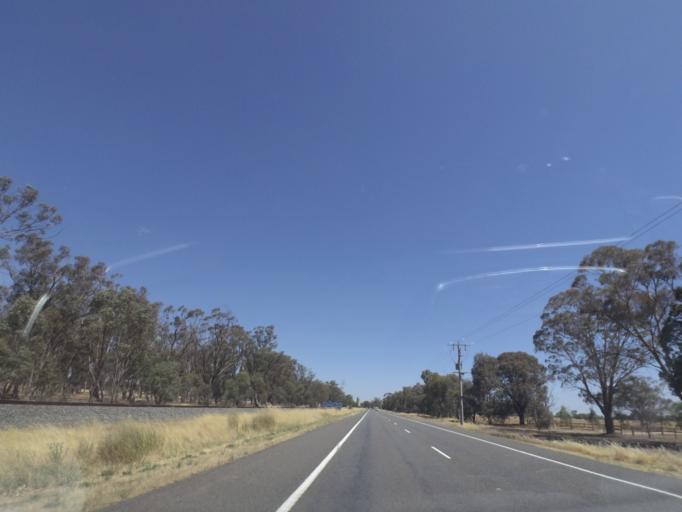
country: AU
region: Victoria
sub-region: Greater Shepparton
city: Shepparton
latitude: -36.2284
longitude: 145.4318
